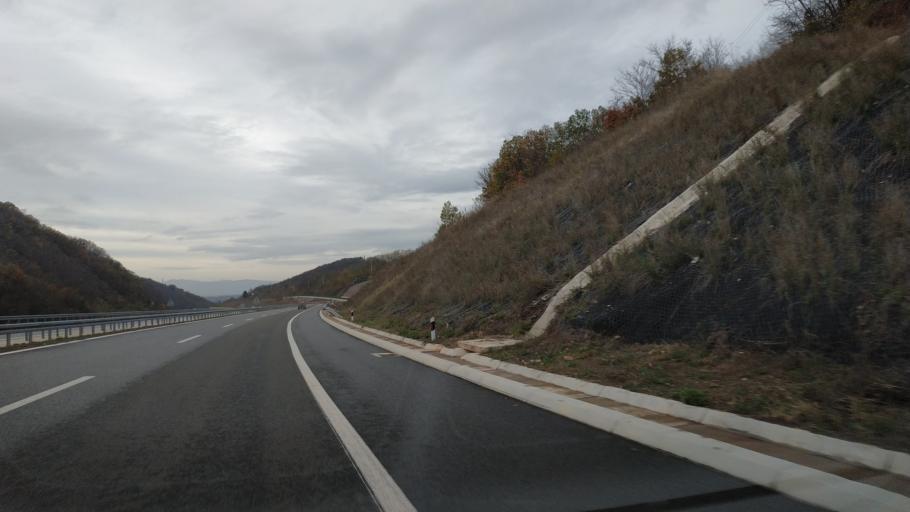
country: RS
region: Central Serbia
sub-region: Nisavski Okrug
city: Niska Banja
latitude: 43.2964
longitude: 22.0810
